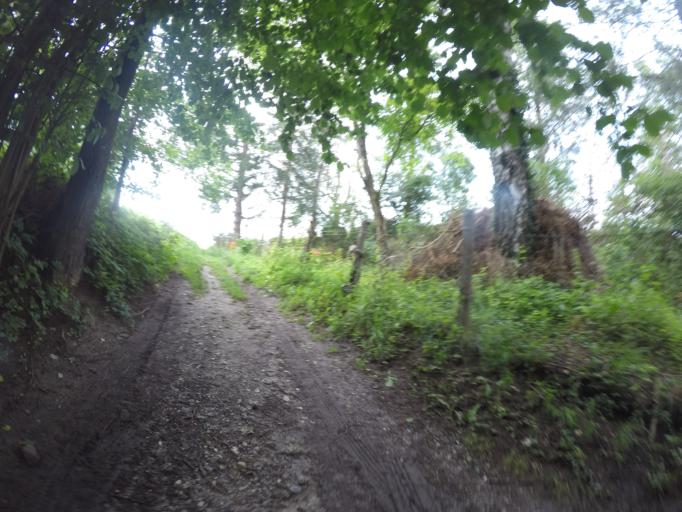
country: DE
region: Bavaria
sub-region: Lower Bavaria
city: Landshut
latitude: 48.5180
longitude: 12.1354
